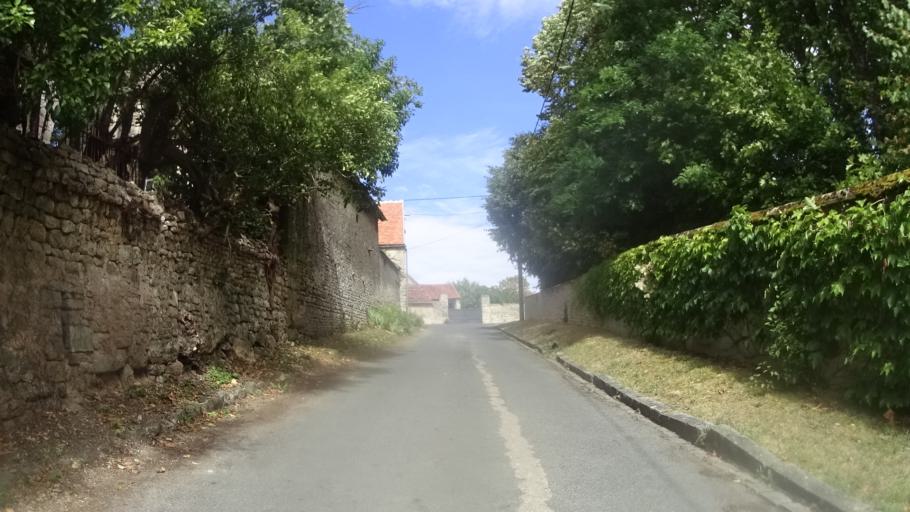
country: FR
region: Centre
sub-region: Departement du Loiret
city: Malesherbes
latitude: 48.2042
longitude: 2.4083
